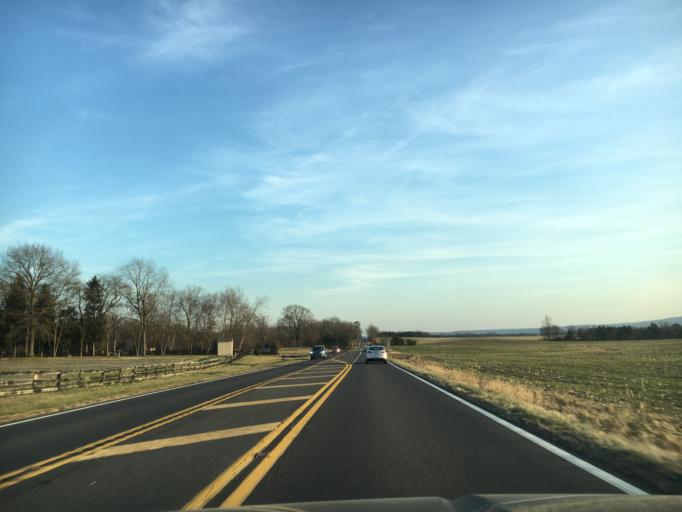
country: US
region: Virginia
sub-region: Culpeper County
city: Culpeper
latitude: 38.4004
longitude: -78.0088
